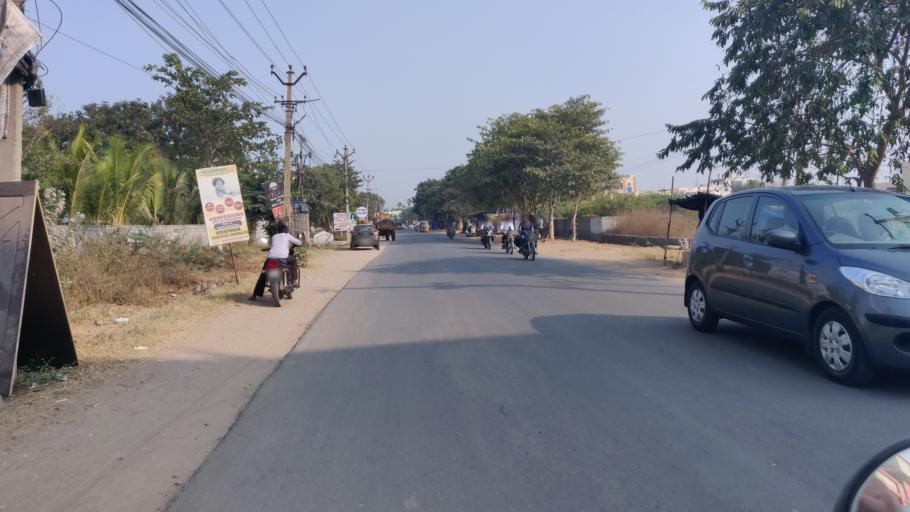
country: IN
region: Telangana
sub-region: Rangareddi
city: Uppal Kalan
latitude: 17.3917
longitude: 78.5992
